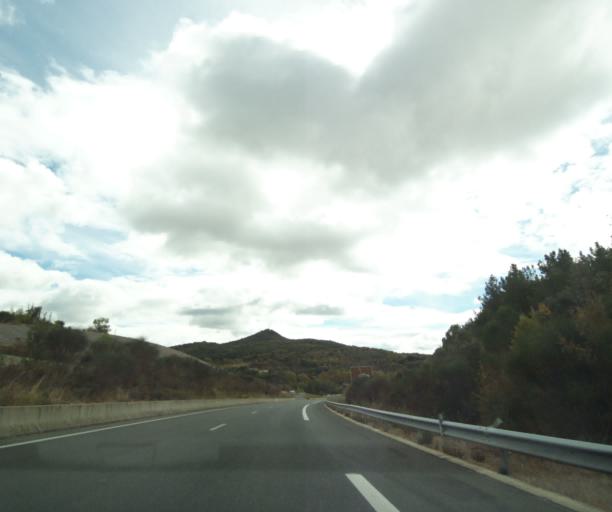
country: FR
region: Languedoc-Roussillon
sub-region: Departement de l'Herault
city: Lodeve
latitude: 43.7707
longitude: 3.3356
